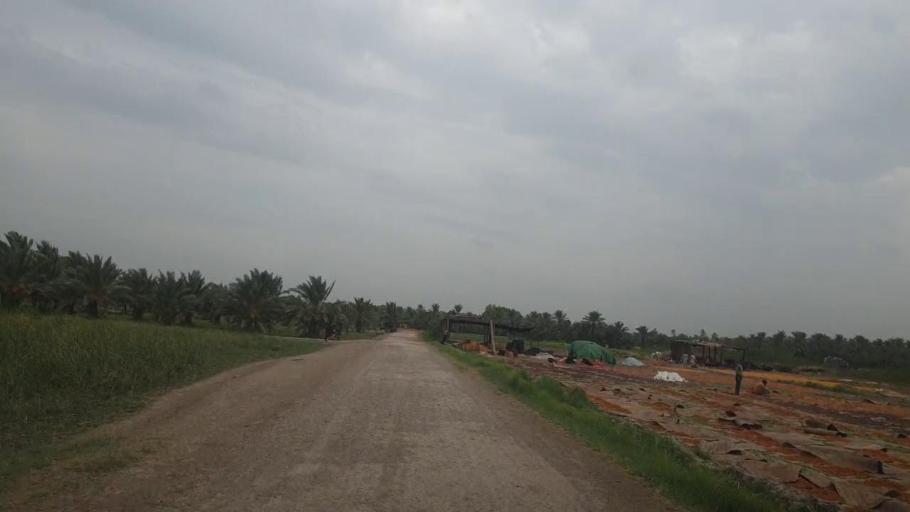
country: PK
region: Sindh
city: Khairpur
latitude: 27.5902
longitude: 68.7404
